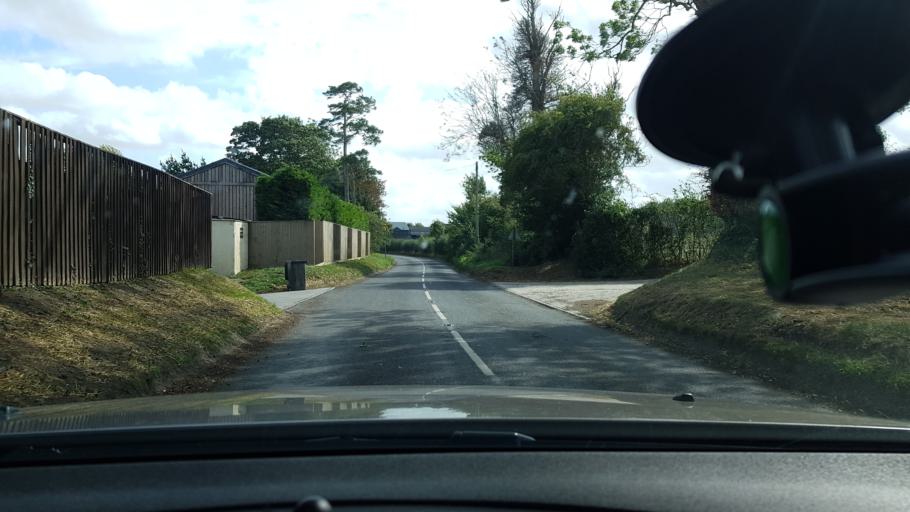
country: GB
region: England
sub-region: West Berkshire
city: Lambourn
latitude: 51.5196
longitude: -1.5476
